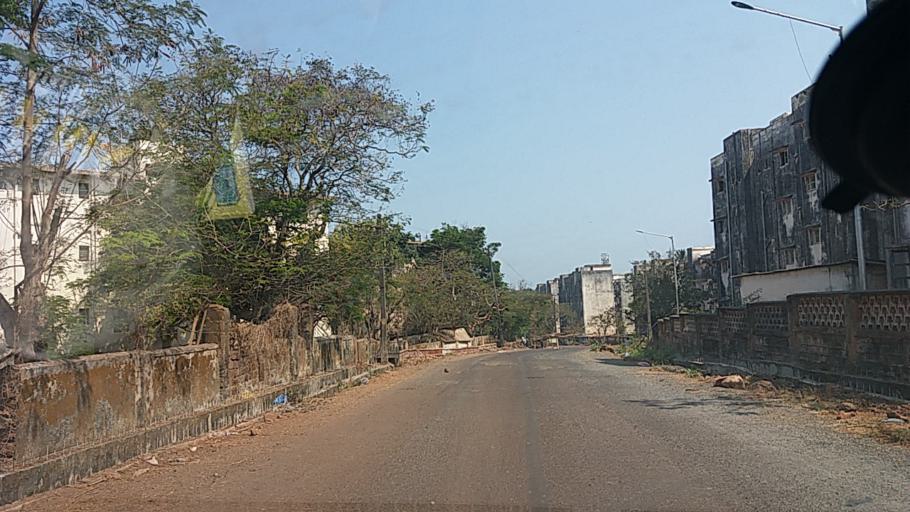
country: IN
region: Goa
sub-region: South Goa
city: Marmagao
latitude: 15.4043
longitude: 73.7893
